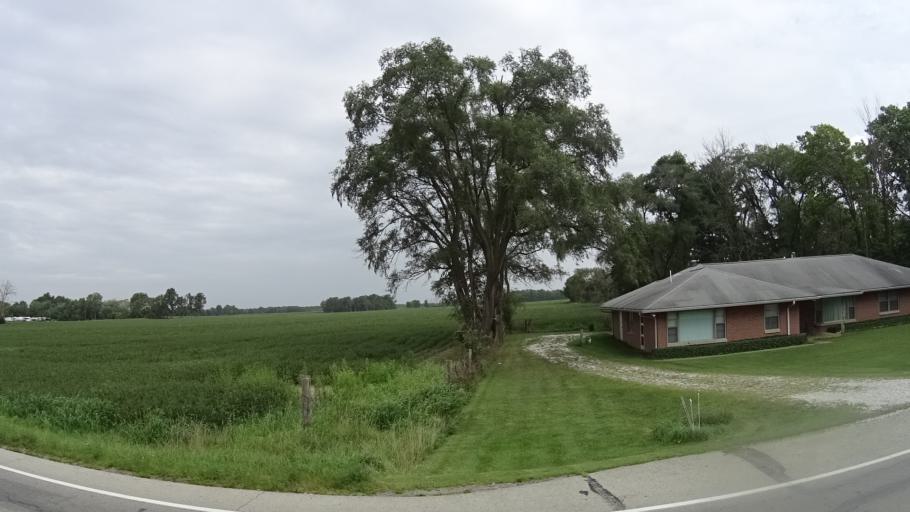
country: US
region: Indiana
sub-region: Madison County
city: Edgewood
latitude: 40.1012
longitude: -85.7559
